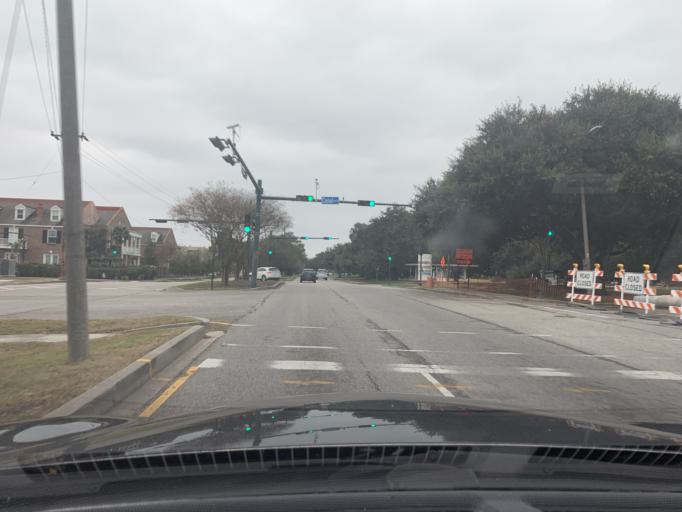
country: US
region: Louisiana
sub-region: Jefferson Parish
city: Metairie
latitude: 30.0195
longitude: -90.1059
